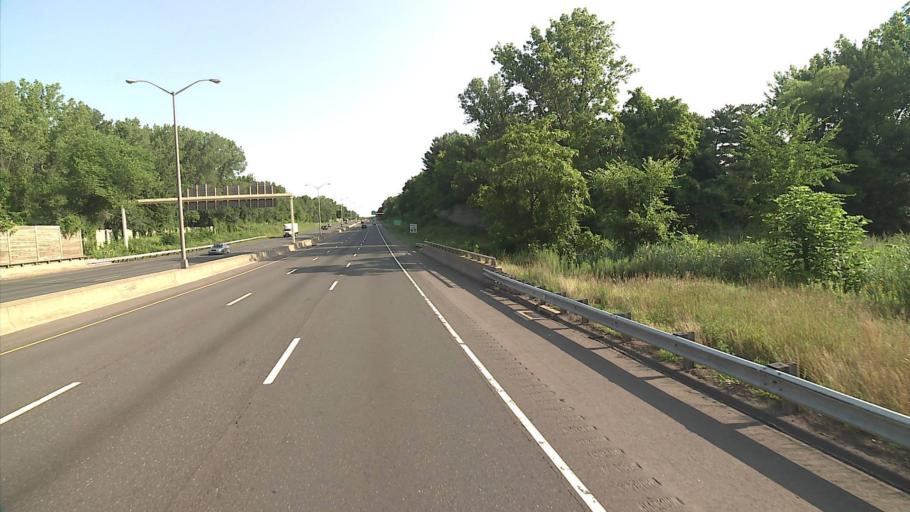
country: US
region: Connecticut
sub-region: Hartford County
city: Thompsonville
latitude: 42.0067
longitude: -72.5853
